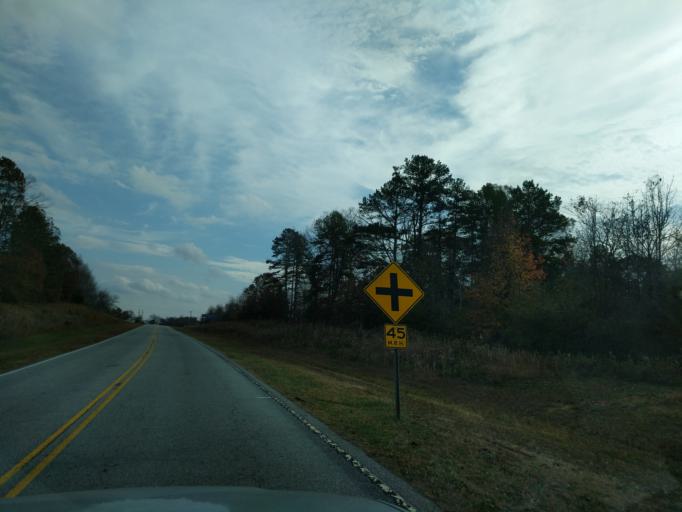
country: US
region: Georgia
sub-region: Franklin County
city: Gumlog
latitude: 34.5564
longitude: -83.0525
